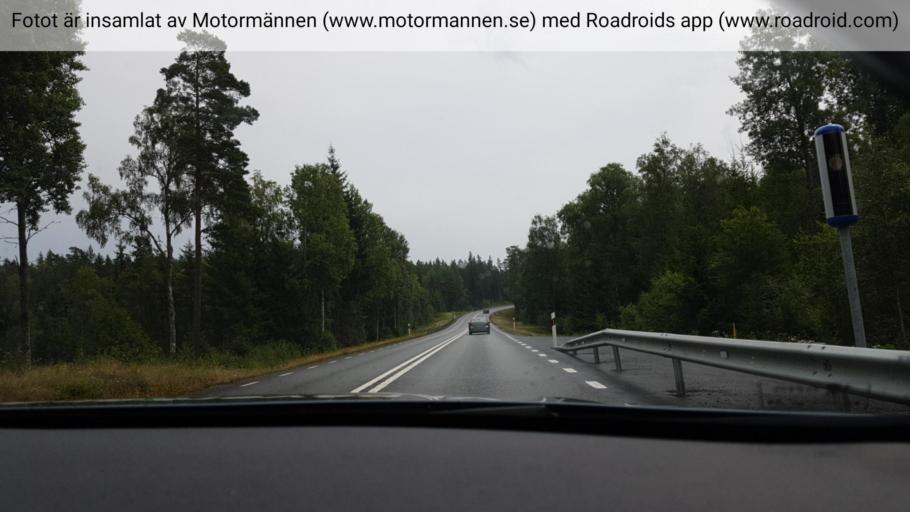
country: SE
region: Joenkoeping
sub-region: Savsjo Kommun
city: Vrigstad
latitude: 57.3999
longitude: 14.3713
